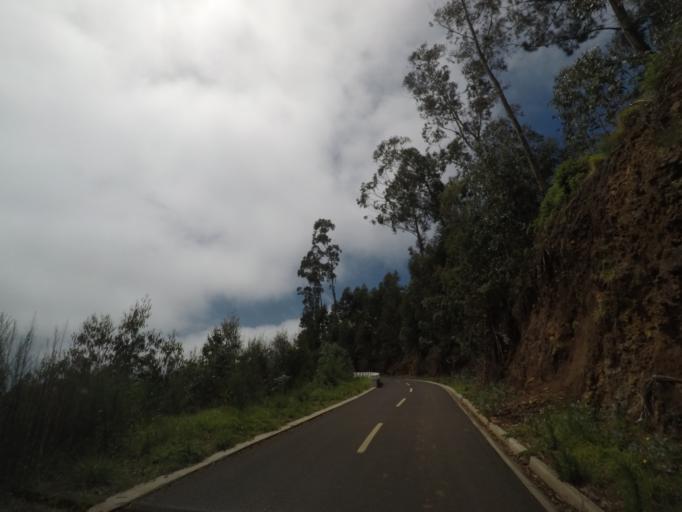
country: PT
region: Madeira
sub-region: Calheta
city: Arco da Calheta
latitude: 32.7245
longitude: -17.1202
